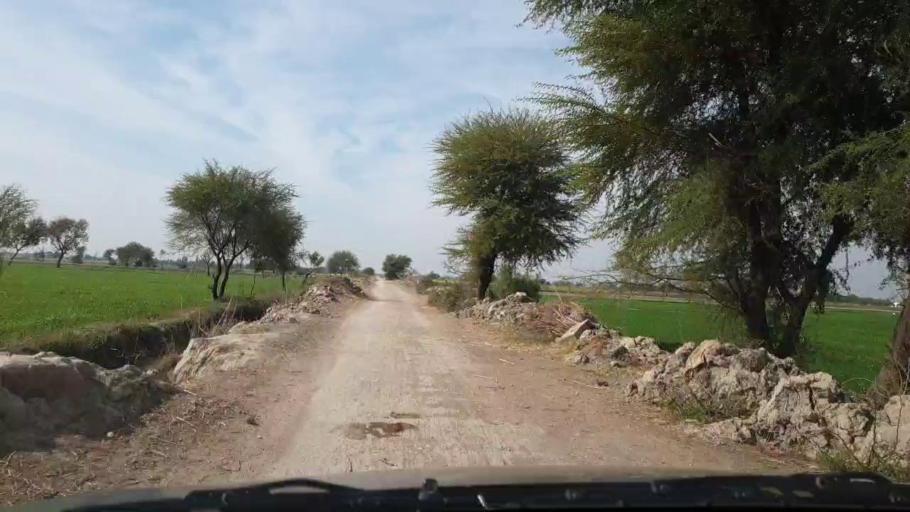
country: PK
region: Sindh
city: Jam Sahib
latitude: 26.2802
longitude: 68.6873
